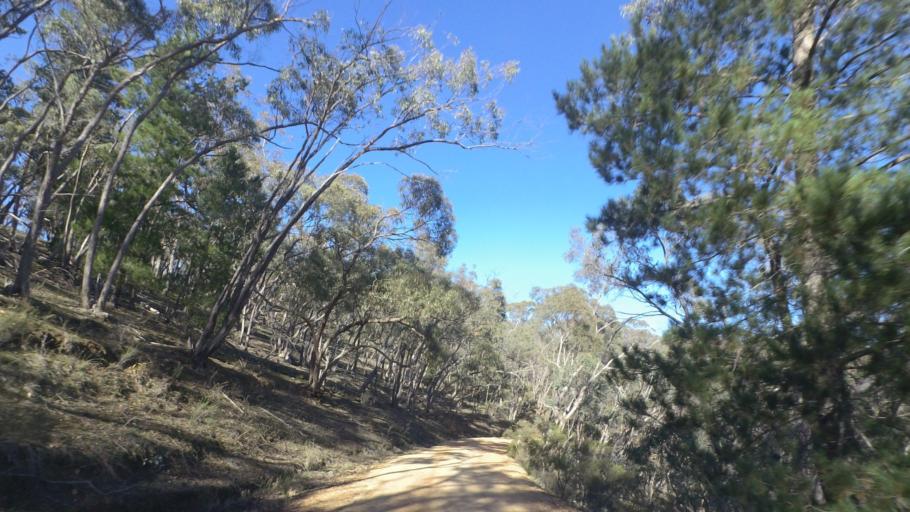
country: AU
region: Victoria
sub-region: Mount Alexander
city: Castlemaine
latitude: -37.0323
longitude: 144.2714
